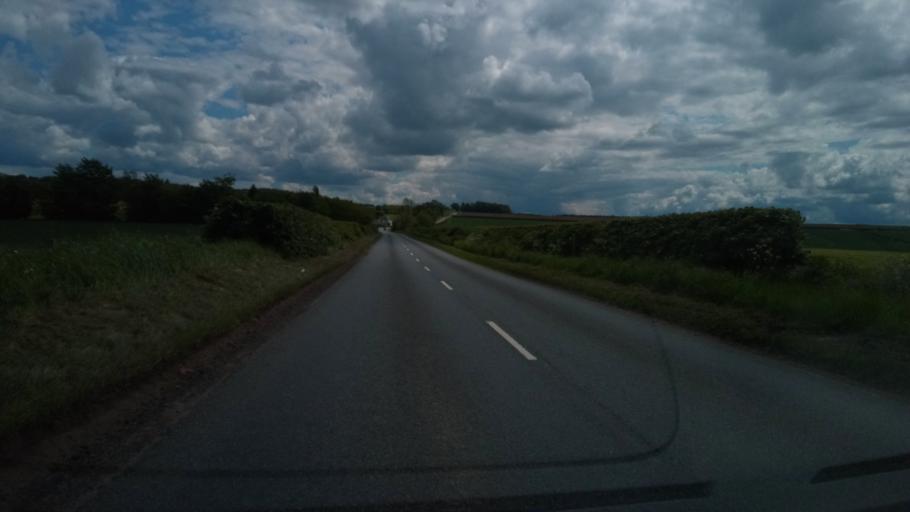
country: GB
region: Scotland
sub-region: The Scottish Borders
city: Kelso
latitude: 55.5808
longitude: -2.4111
